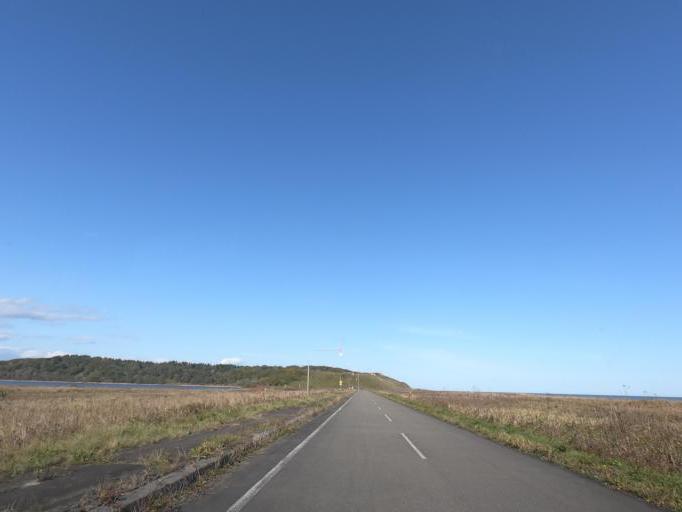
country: JP
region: Hokkaido
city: Obihiro
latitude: 42.5980
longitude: 143.5478
